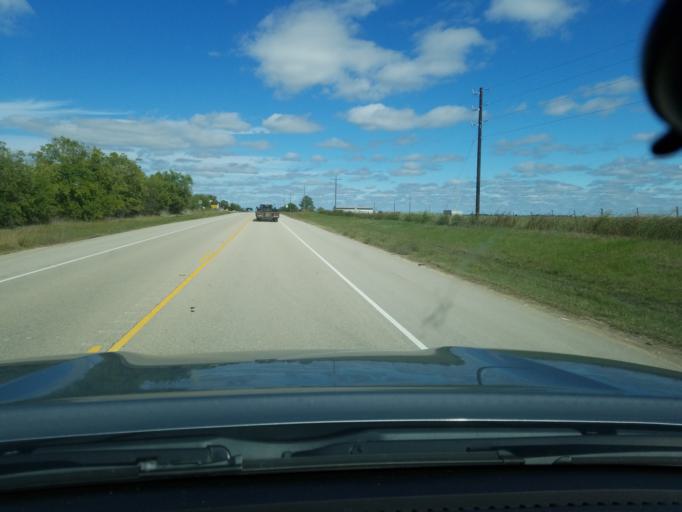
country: US
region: Texas
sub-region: Hamilton County
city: Hamilton
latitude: 31.6633
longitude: -98.1409
